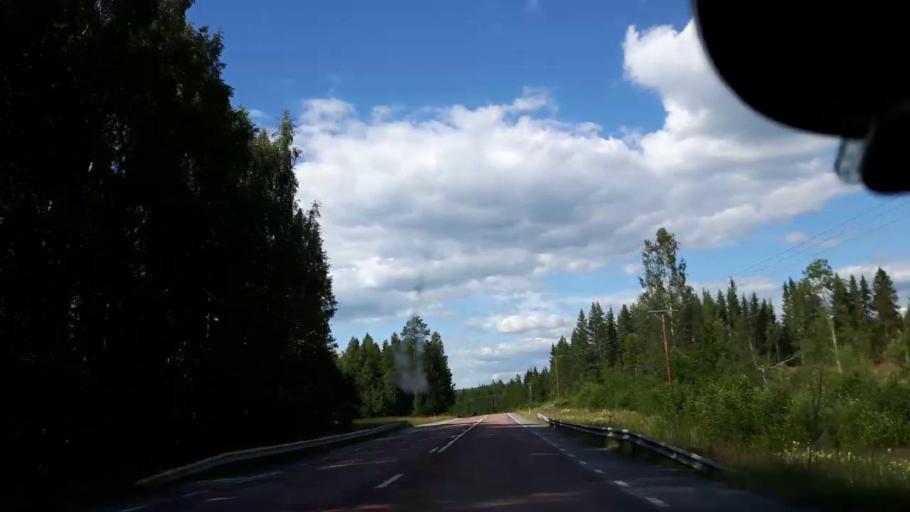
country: SE
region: Jaemtland
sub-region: Braecke Kommun
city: Braecke
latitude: 62.8051
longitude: 15.3696
